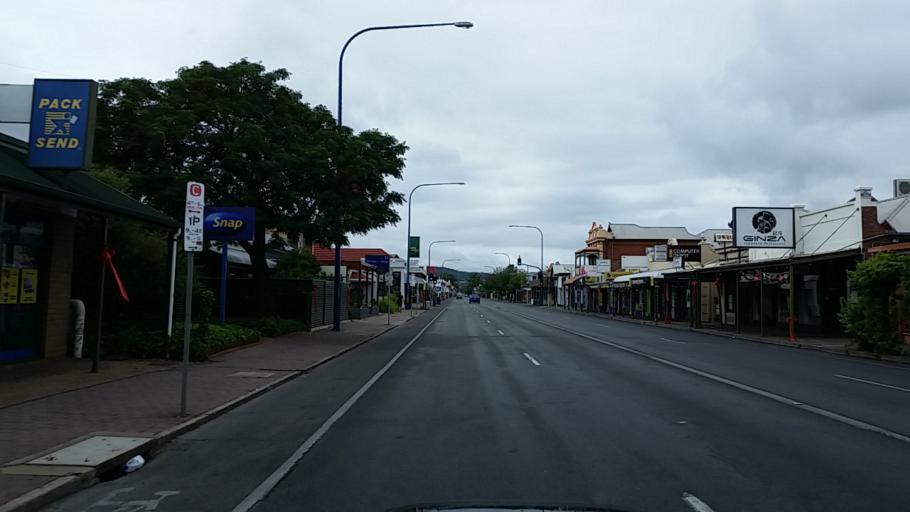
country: AU
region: South Australia
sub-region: Unley
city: Unley
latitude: -34.9433
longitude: 138.6070
